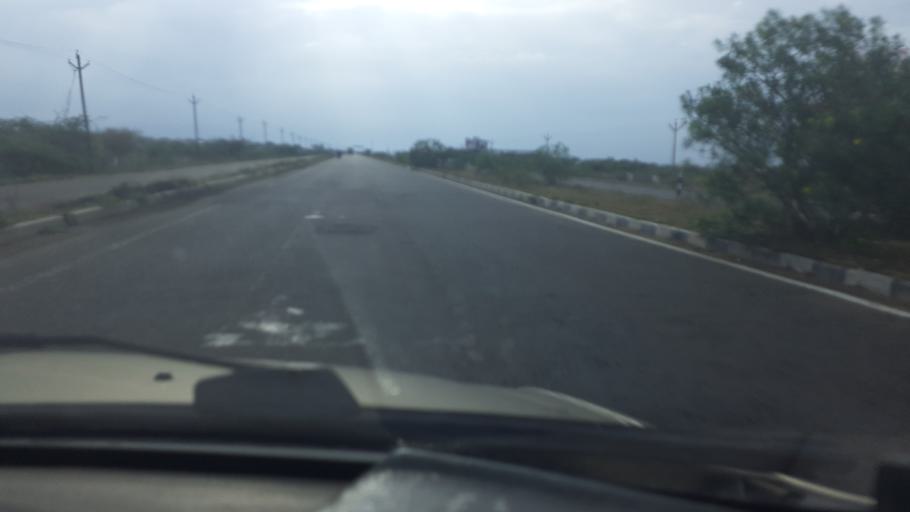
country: IN
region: Tamil Nadu
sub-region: Tirunelveli Kattabo
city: Tirunelveli
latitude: 8.6639
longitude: 77.7302
